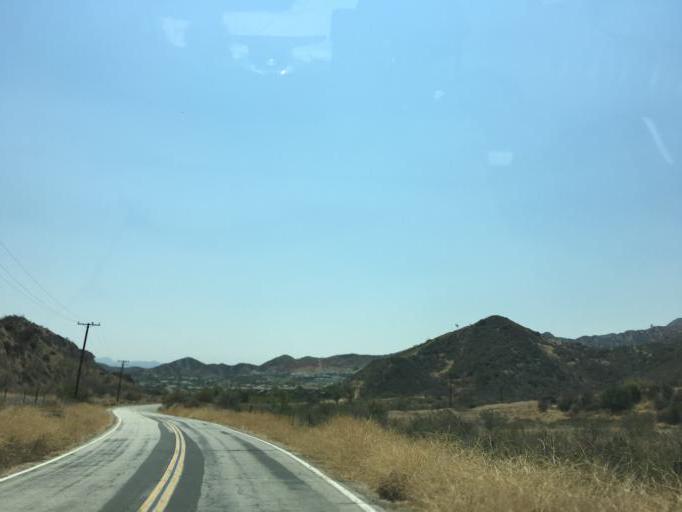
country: US
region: California
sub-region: Los Angeles County
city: Santa Clarita
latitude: 34.3794
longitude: -118.5976
